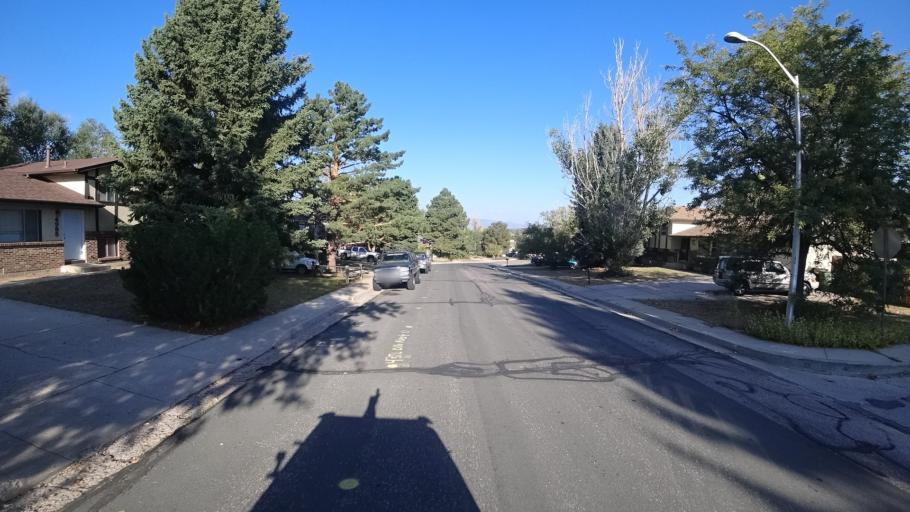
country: US
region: Colorado
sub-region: El Paso County
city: Cimarron Hills
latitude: 38.8873
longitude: -104.7357
